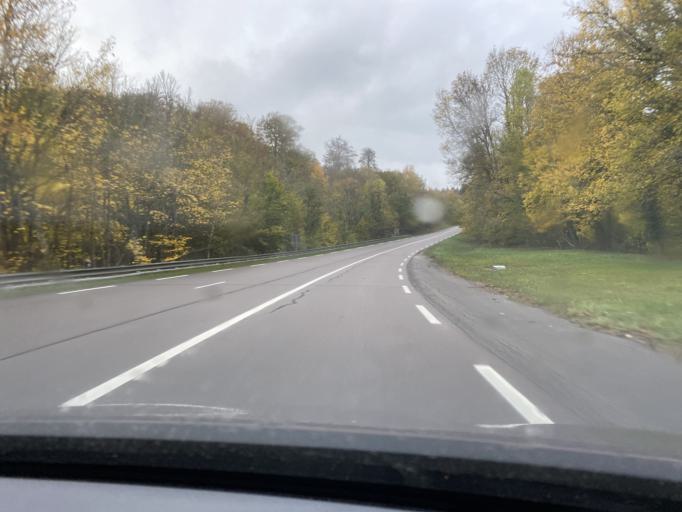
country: FR
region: Bourgogne
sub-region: Departement de la Cote-d'Or
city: Saulieu
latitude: 47.3016
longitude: 4.2105
